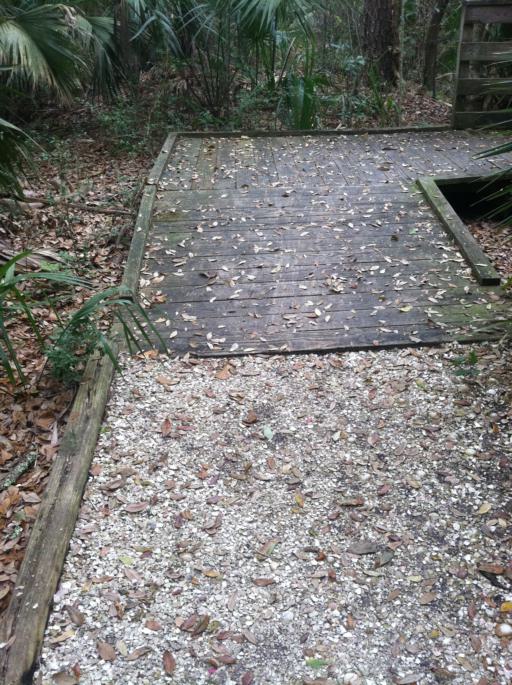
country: US
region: Florida
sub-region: Franklin County
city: Apalachicola
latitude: 29.7324
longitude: -84.9969
